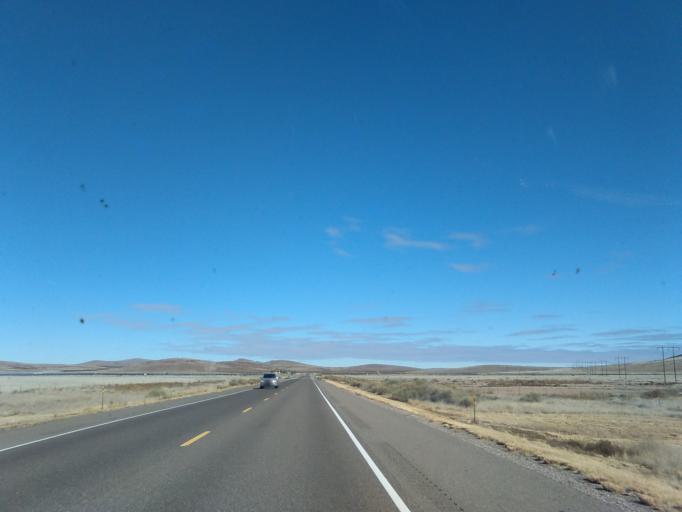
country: US
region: New Mexico
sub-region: Dona Ana County
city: Hatch
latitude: 32.5645
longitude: -107.4652
